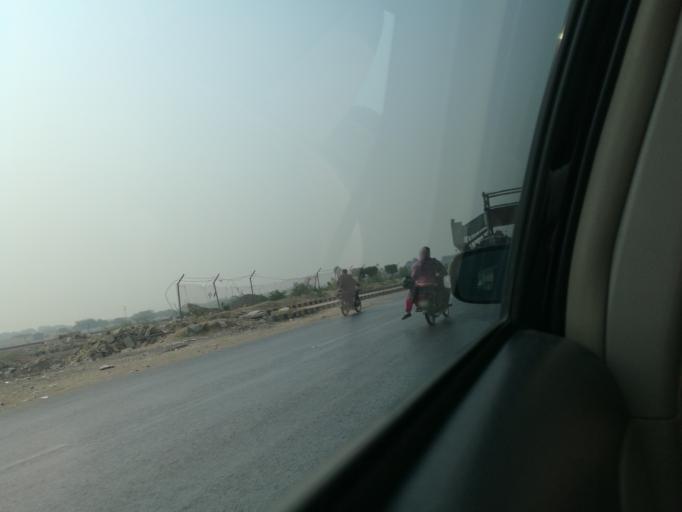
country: PK
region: Sindh
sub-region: Karachi District
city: Karachi
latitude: 24.8766
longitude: 67.1021
